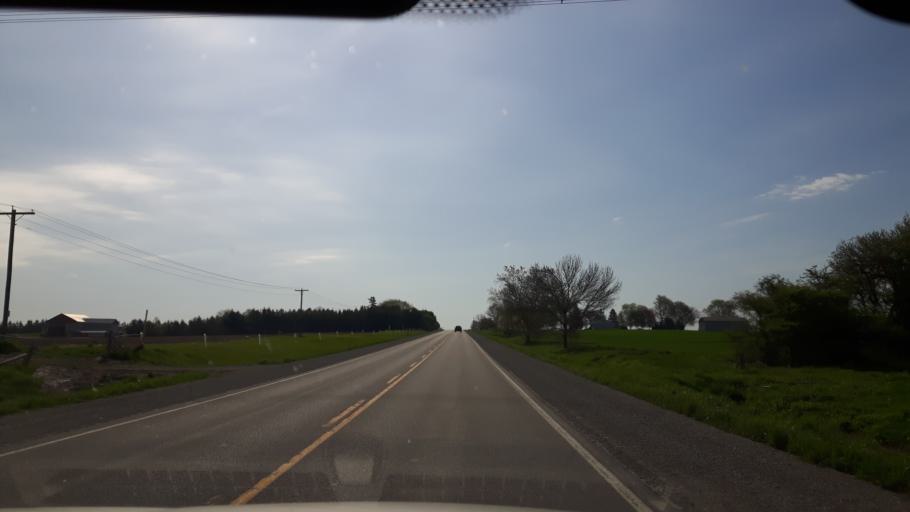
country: CA
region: Ontario
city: Bluewater
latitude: 43.5429
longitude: -81.6346
